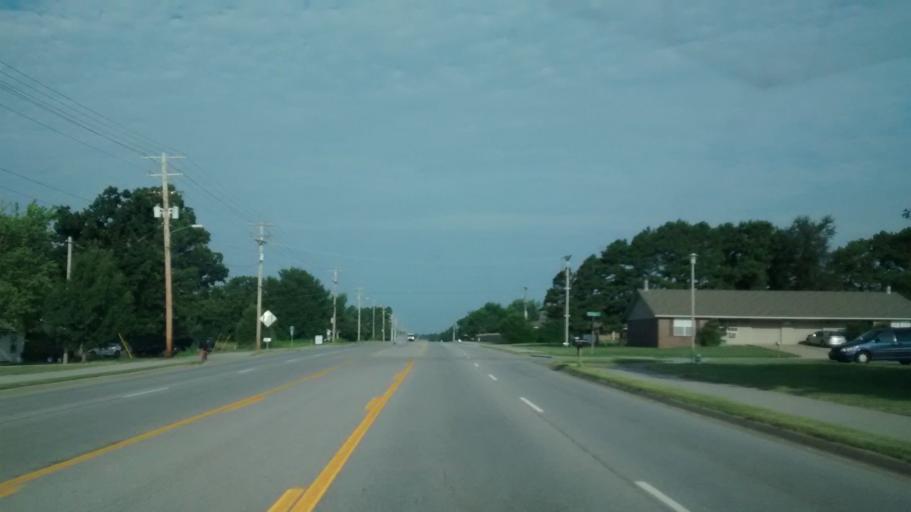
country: US
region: Arkansas
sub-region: Washington County
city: Farmington
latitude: 36.0789
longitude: -94.2247
